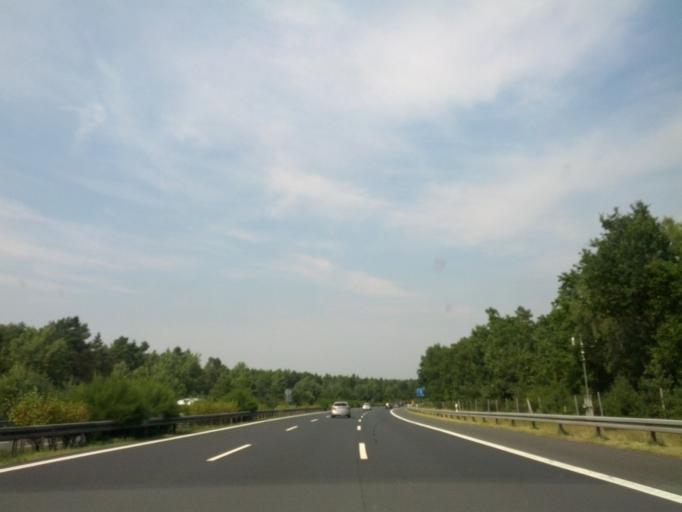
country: DE
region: Brandenburg
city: Fichtenwalde
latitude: 52.2557
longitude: 12.9090
